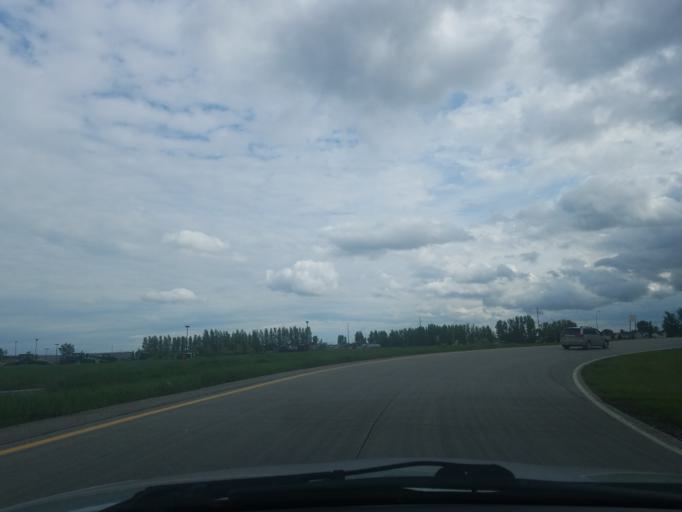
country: US
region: Minnesota
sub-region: Clay County
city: Dilworth
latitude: 46.8466
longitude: -96.7177
